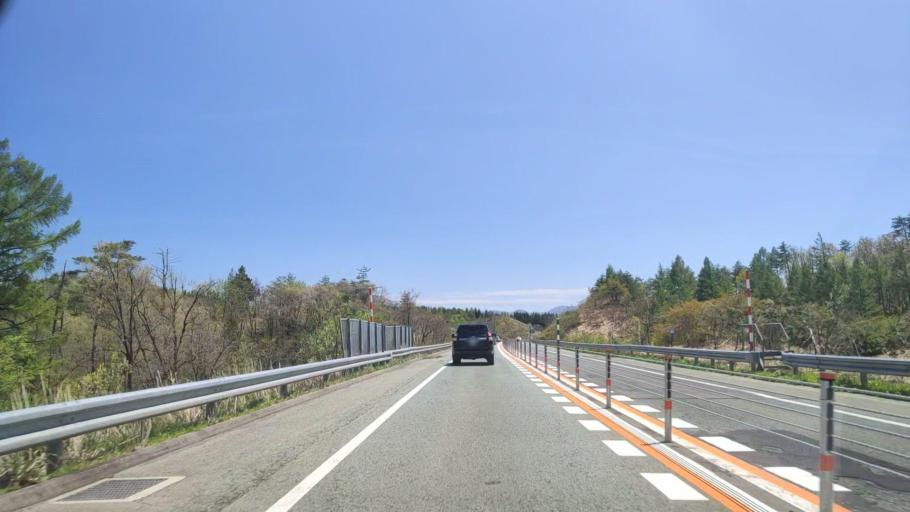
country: JP
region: Yamagata
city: Obanazawa
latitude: 38.6510
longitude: 140.3703
